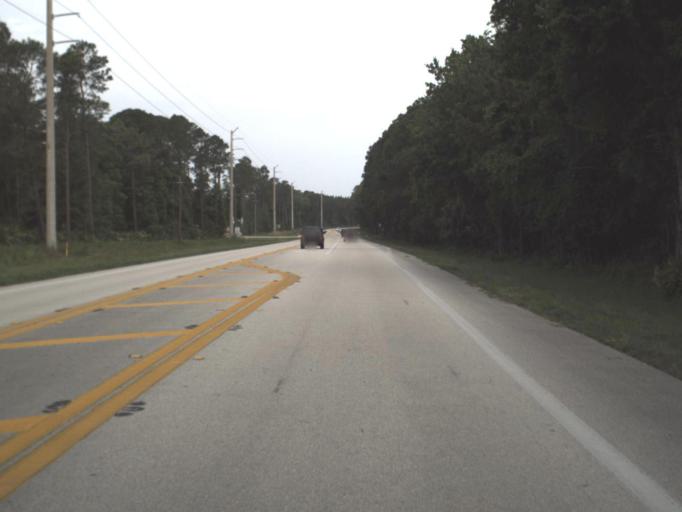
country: US
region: Florida
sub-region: Saint Johns County
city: Saint Augustine
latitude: 29.9306
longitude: -81.4271
